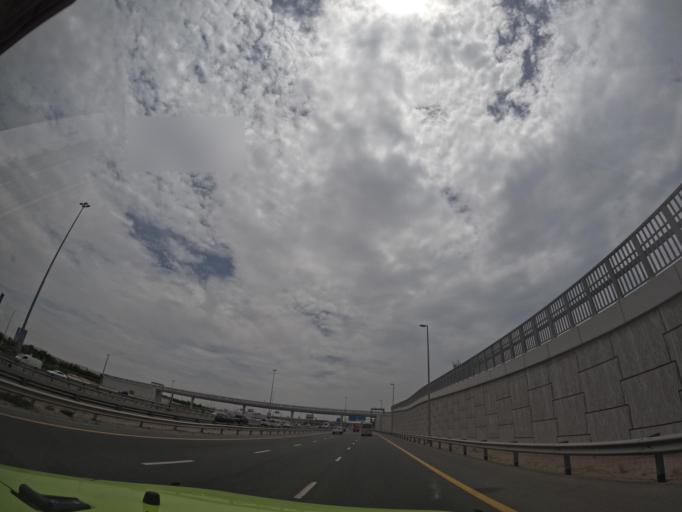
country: AE
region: Dubai
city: Dubai
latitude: 25.1743
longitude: 55.2712
